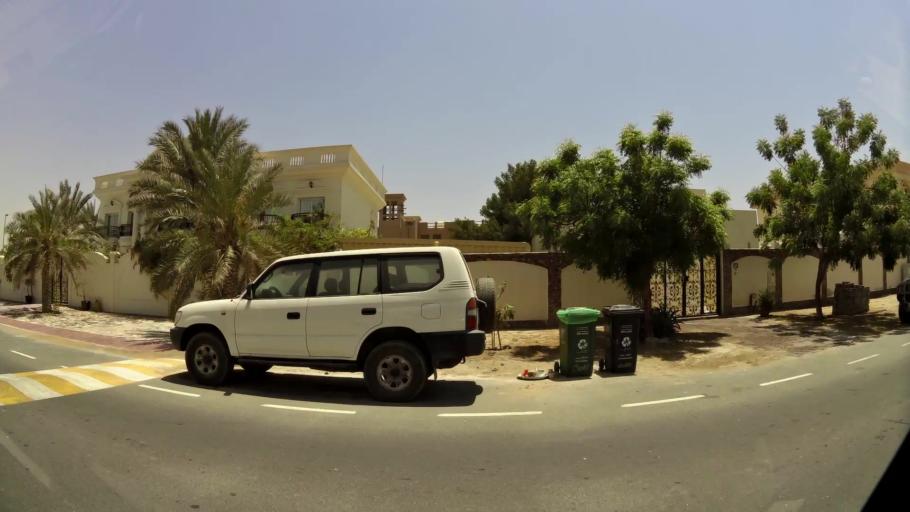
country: AE
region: Dubai
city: Dubai
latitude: 25.0845
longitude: 55.2084
